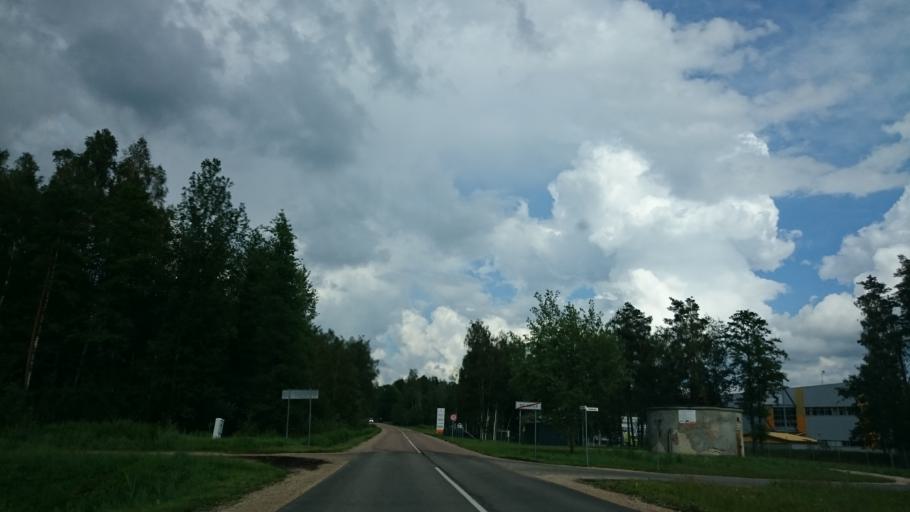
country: LV
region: Salaspils
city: Salaspils
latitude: 56.8666
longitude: 24.3793
